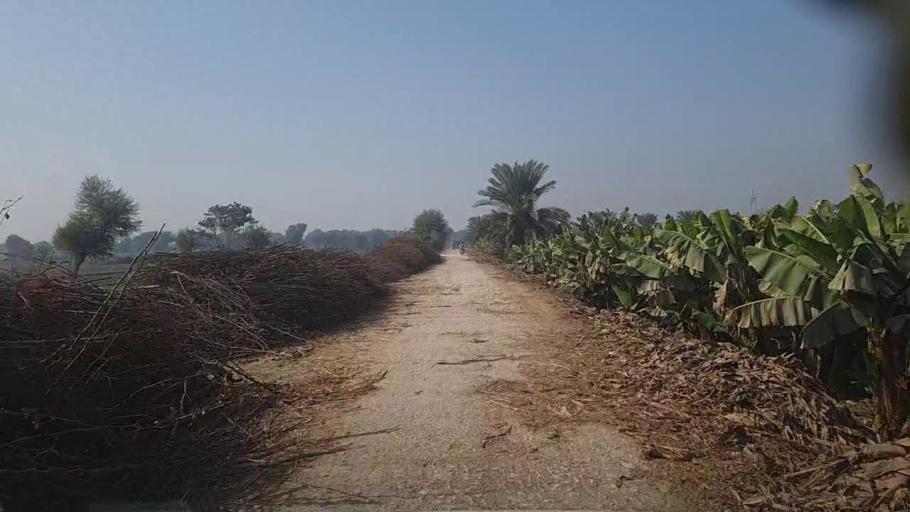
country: PK
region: Sindh
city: Kandiari
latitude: 26.9680
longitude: 68.4609
